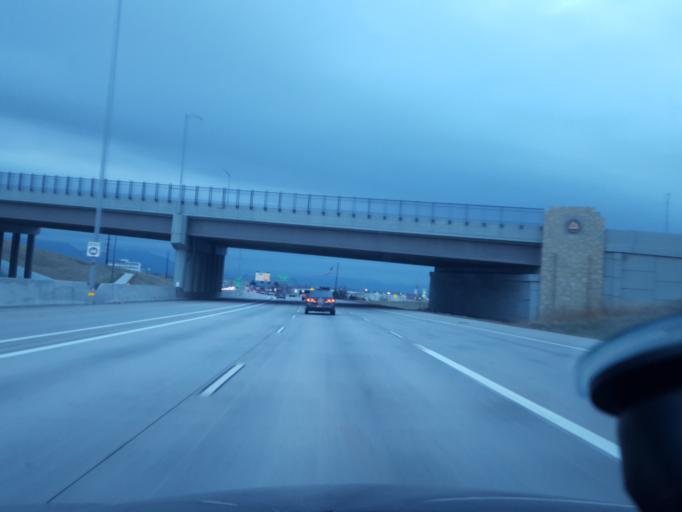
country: US
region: Colorado
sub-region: Broomfield County
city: Broomfield
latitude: 39.9160
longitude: -105.0932
